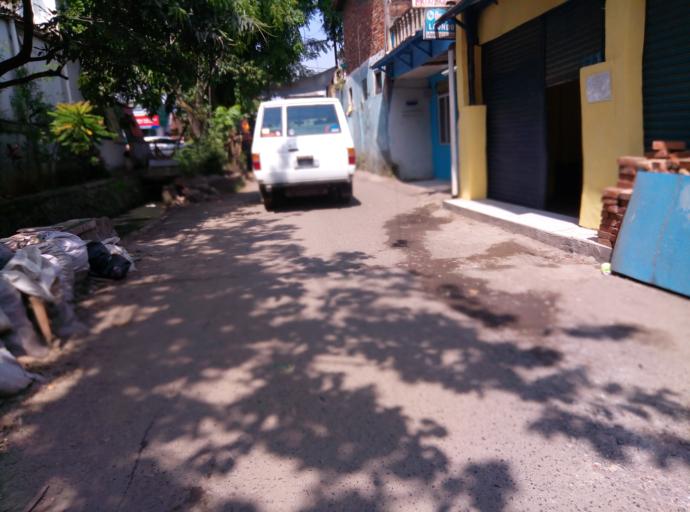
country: ID
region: West Java
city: Bandung
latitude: -6.9328
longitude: 107.6455
